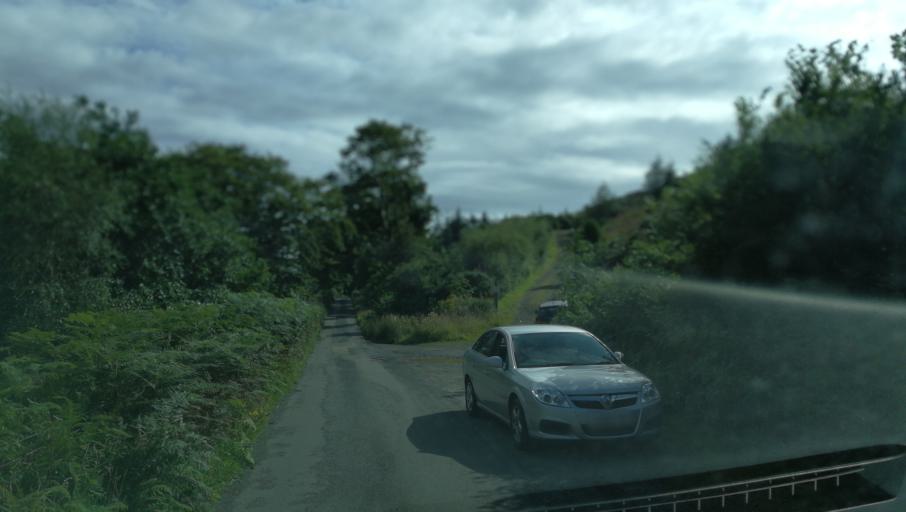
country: GB
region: Scotland
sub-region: Highland
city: Isle of Skye
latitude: 57.4002
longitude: -6.5678
